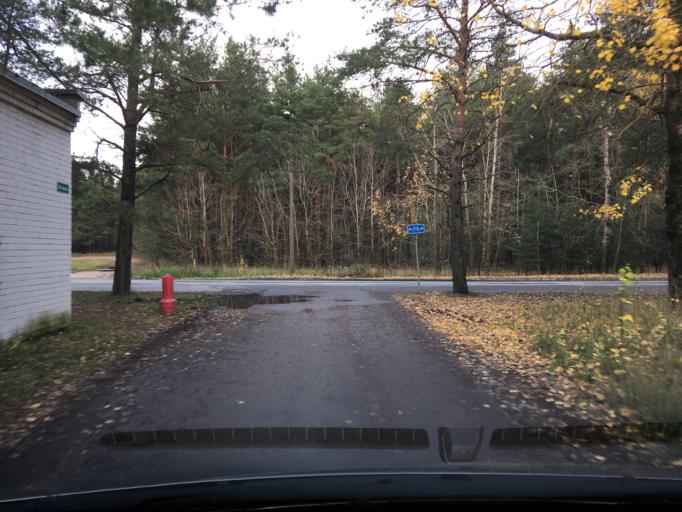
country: EE
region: Harju
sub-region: Tallinna linn
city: Tallinn
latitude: 59.3760
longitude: 24.7409
